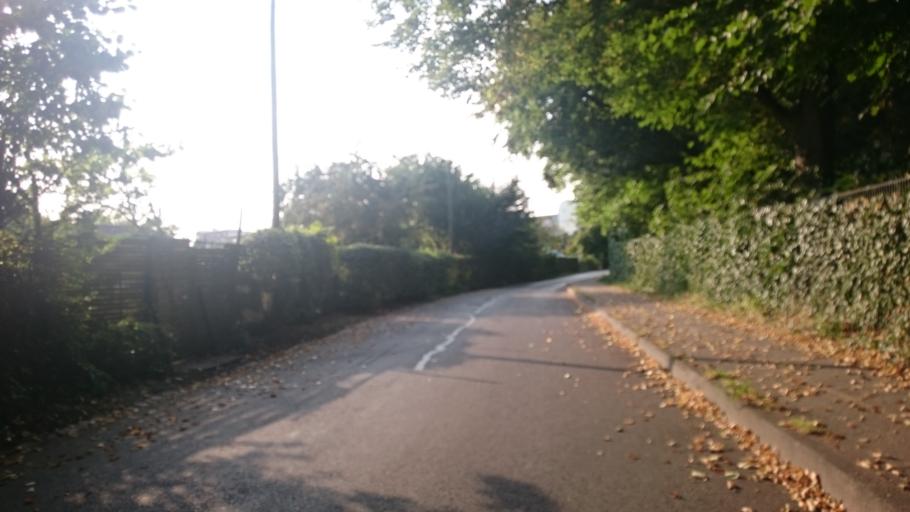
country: DE
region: Hamburg
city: Stellingen
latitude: 53.5708
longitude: 9.9272
